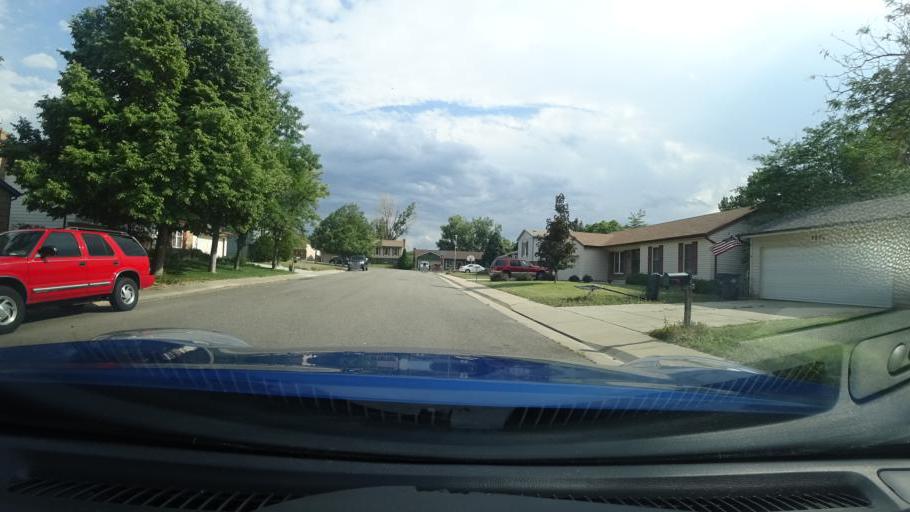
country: US
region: Colorado
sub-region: Adams County
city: Aurora
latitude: 39.6904
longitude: -104.7991
